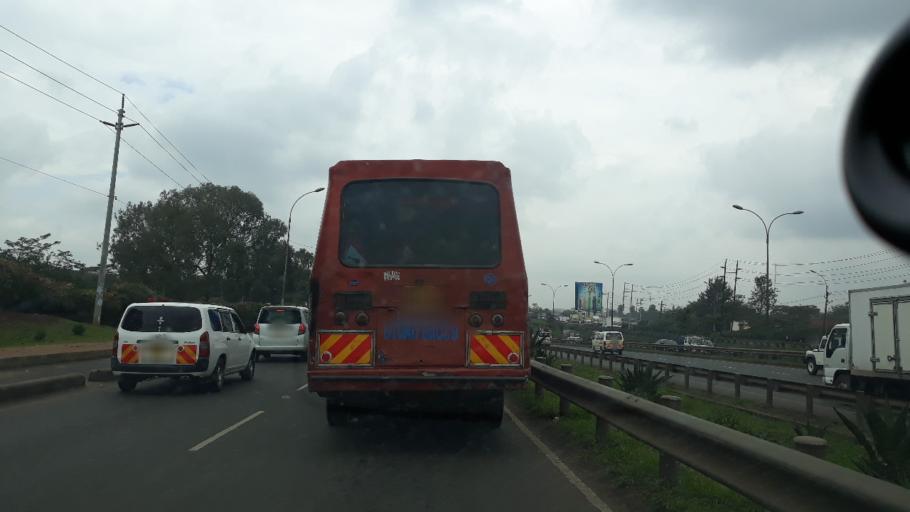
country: KE
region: Nairobi Area
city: Pumwani
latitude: -1.2469
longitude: 36.8647
